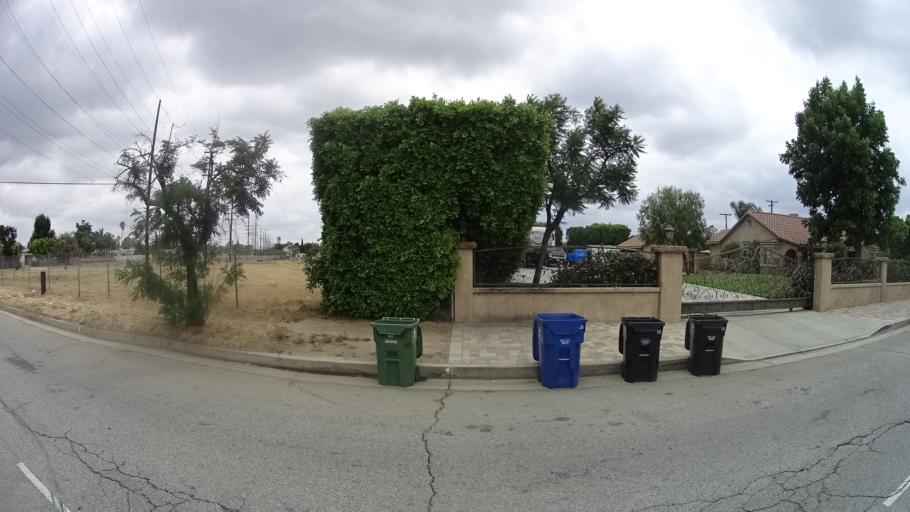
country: US
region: California
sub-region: Los Angeles County
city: San Fernando
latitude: 34.2644
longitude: -118.4559
